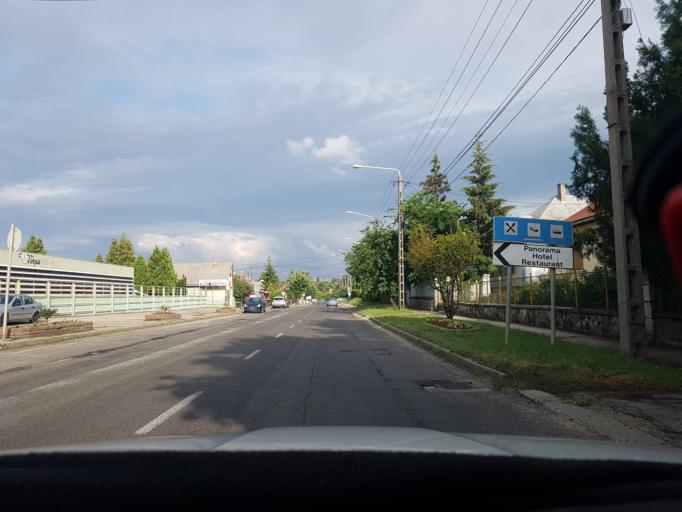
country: HU
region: Komarom-Esztergom
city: Labatlan
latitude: 47.7523
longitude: 18.4756
